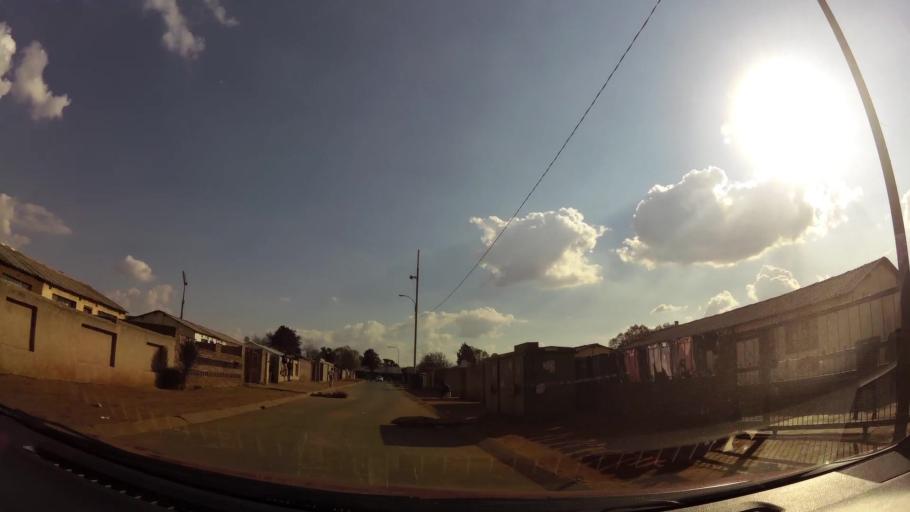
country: ZA
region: Gauteng
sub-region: City of Johannesburg Metropolitan Municipality
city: Soweto
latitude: -26.2245
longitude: 27.8655
